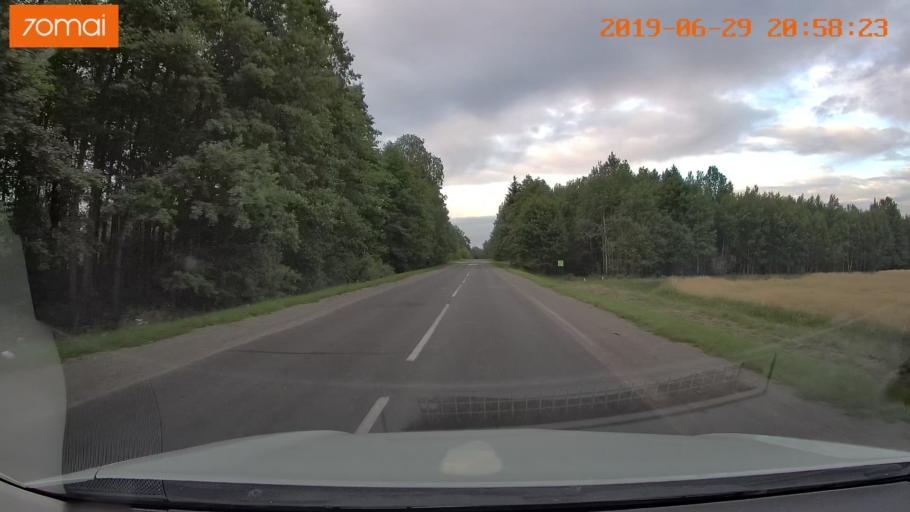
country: BY
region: Brest
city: Hantsavichy
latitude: 52.7293
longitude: 26.3852
